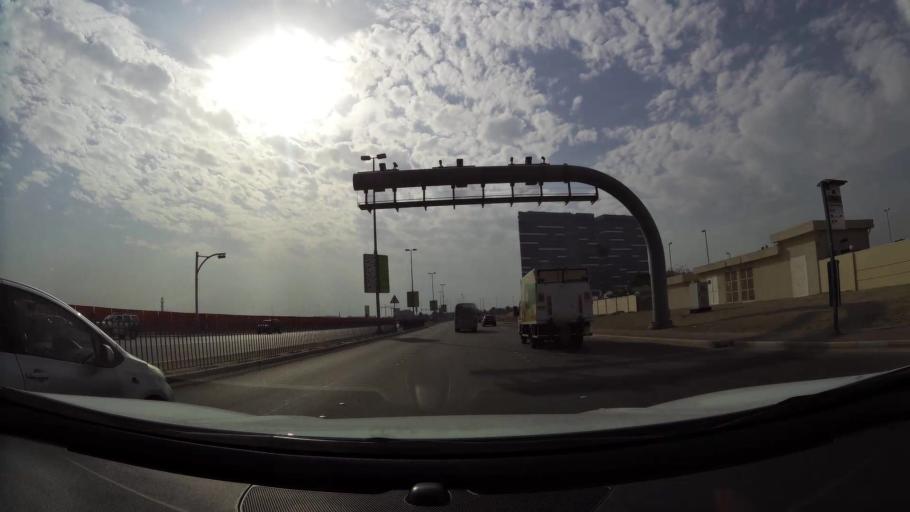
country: AE
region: Abu Dhabi
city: Abu Dhabi
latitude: 24.3743
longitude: 54.5352
